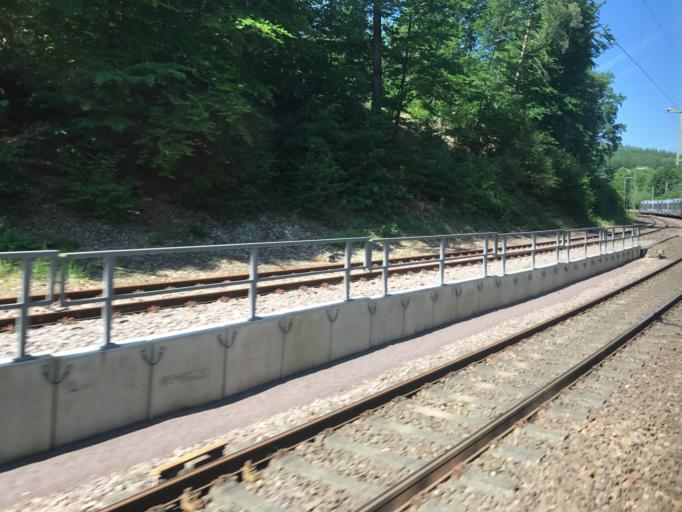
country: DE
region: Saarland
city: Nohfelden
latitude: 49.5835
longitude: 7.1248
